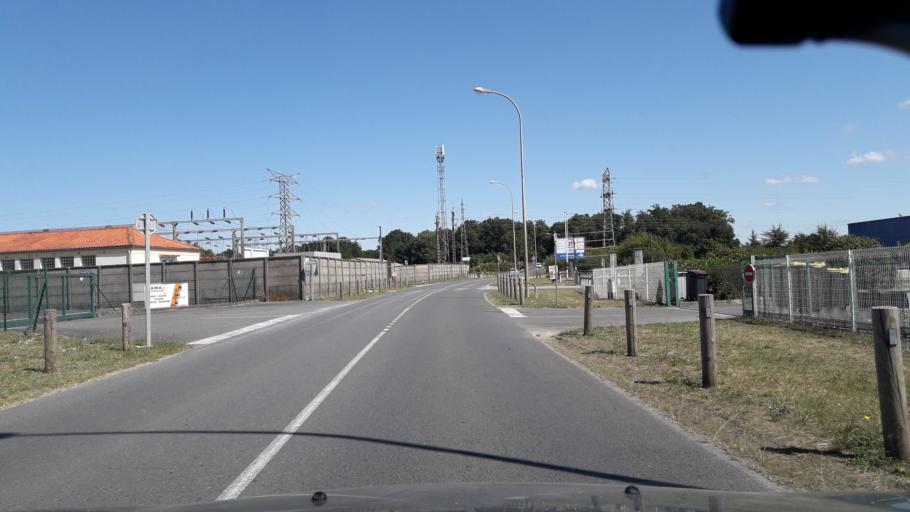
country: FR
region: Poitou-Charentes
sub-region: Departement de la Charente
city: Gond-Pontouvre
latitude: 45.6941
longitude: 0.1856
